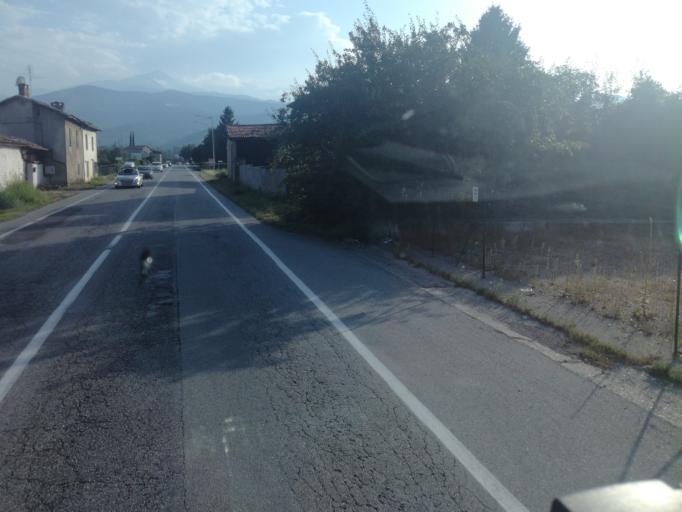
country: IT
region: Piedmont
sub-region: Provincia di Torino
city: Bibiana
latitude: 44.8120
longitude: 7.2934
